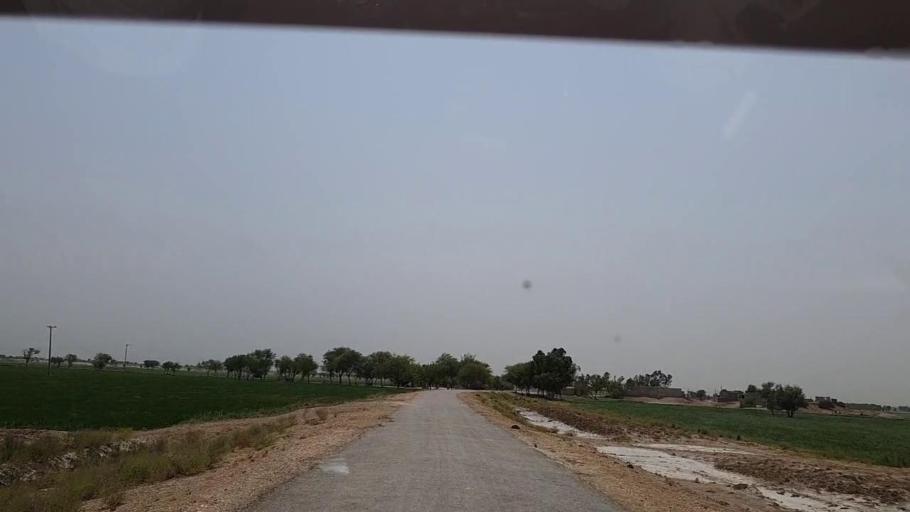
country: PK
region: Sindh
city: Khairpur Nathan Shah
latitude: 27.0123
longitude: 67.6574
